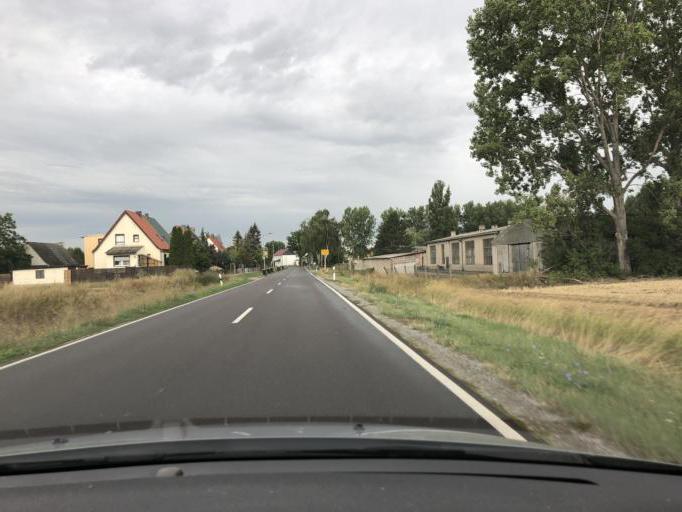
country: DE
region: Saxony-Anhalt
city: Calbe
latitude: 51.8890
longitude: 11.7986
